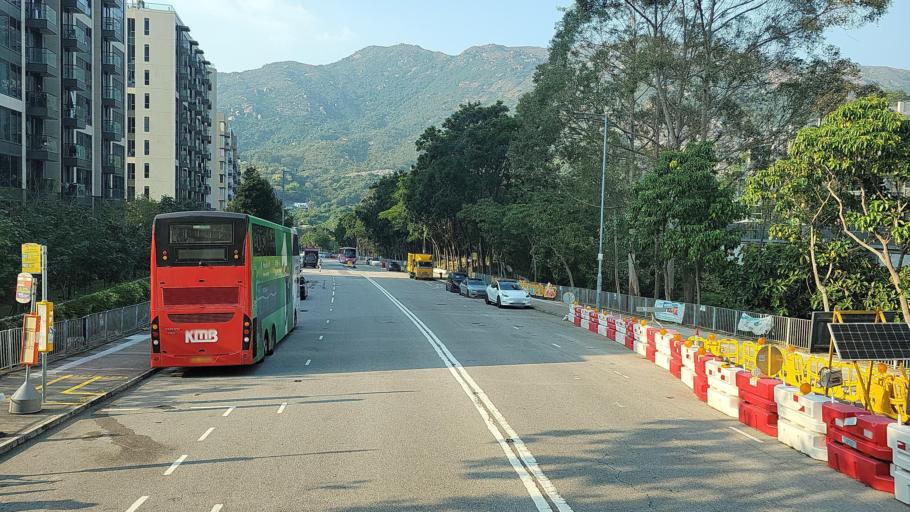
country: HK
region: Tuen Mun
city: Tuen Mun
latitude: 22.3732
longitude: 114.0031
